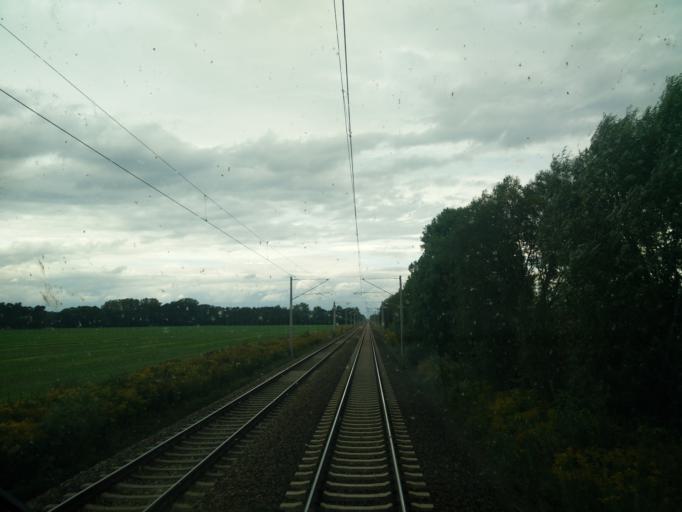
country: DE
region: Brandenburg
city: Luebben
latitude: 51.9715
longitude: 13.8075
